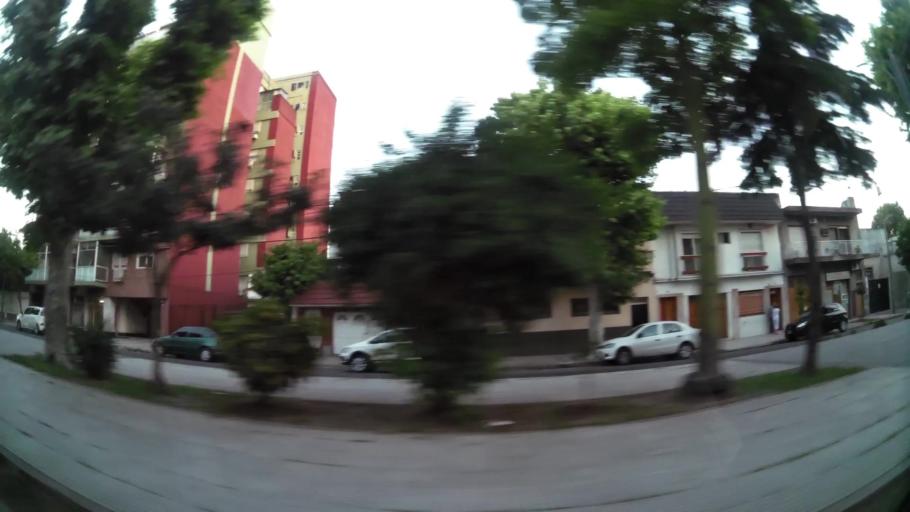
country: AR
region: Buenos Aires F.D.
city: Villa Lugano
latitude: -34.6750
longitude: -58.4728
